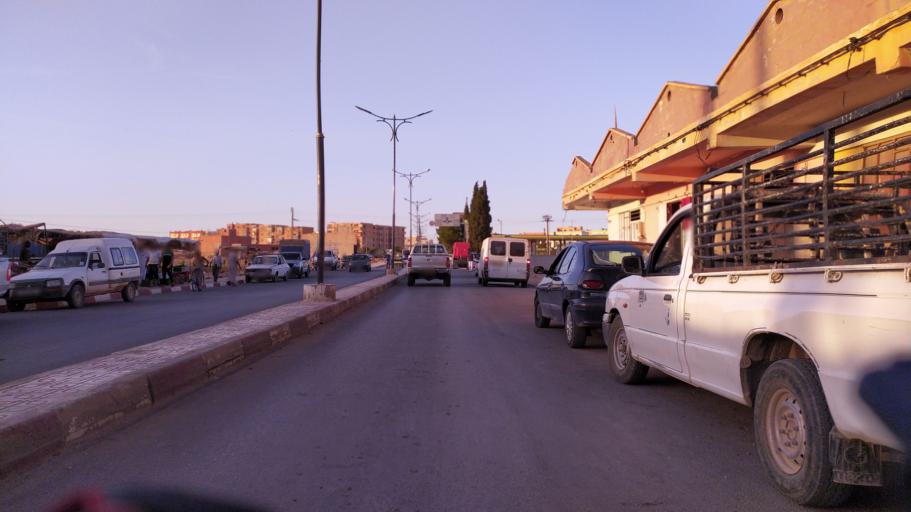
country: DZ
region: Tiaret
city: Frenda
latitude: 34.8947
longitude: 1.2472
